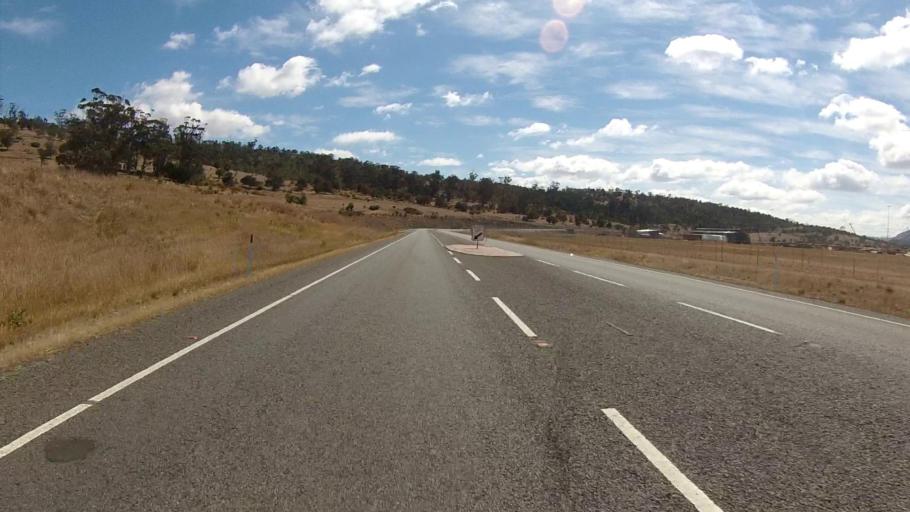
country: AU
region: Tasmania
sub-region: Brighton
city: Bridgewater
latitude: -42.7144
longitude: 147.2278
